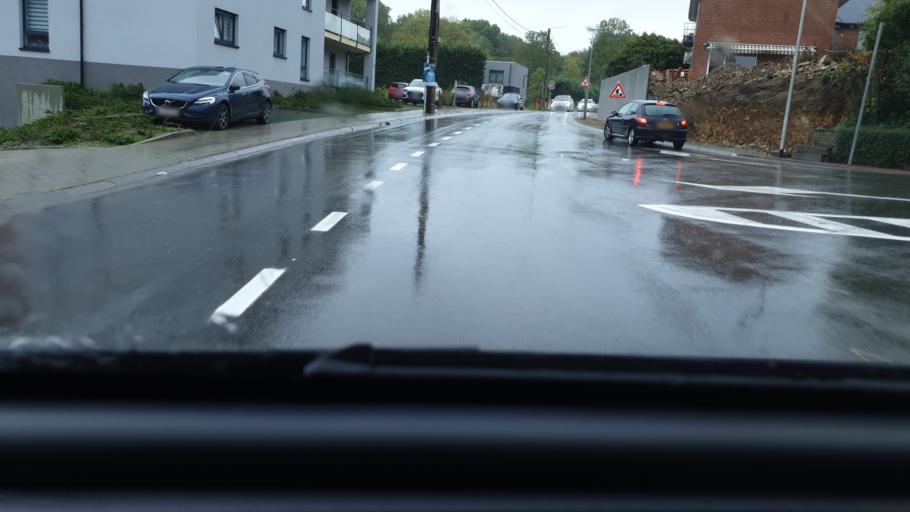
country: BE
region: Wallonia
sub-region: Province du Hainaut
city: Charleroi
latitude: 50.3732
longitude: 4.4763
